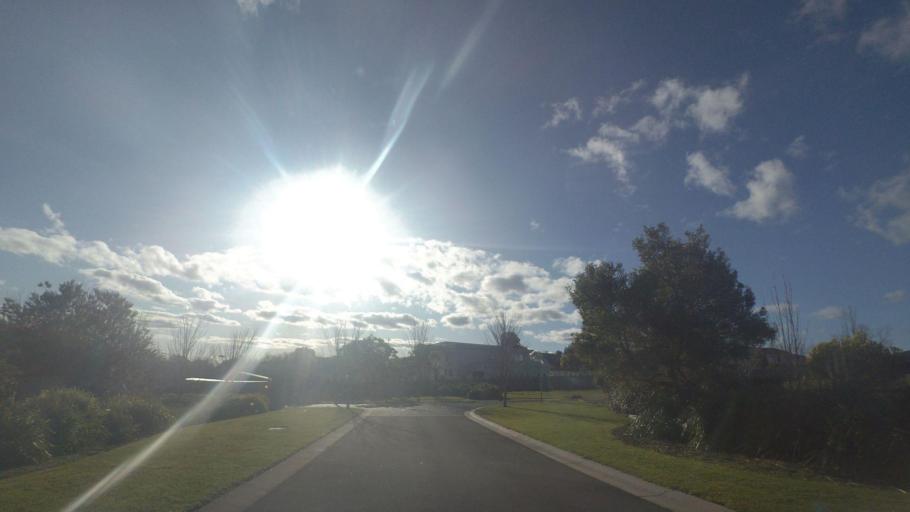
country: AU
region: Victoria
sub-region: Yarra Ranges
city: Lysterfield
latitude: -37.9130
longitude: 145.2893
